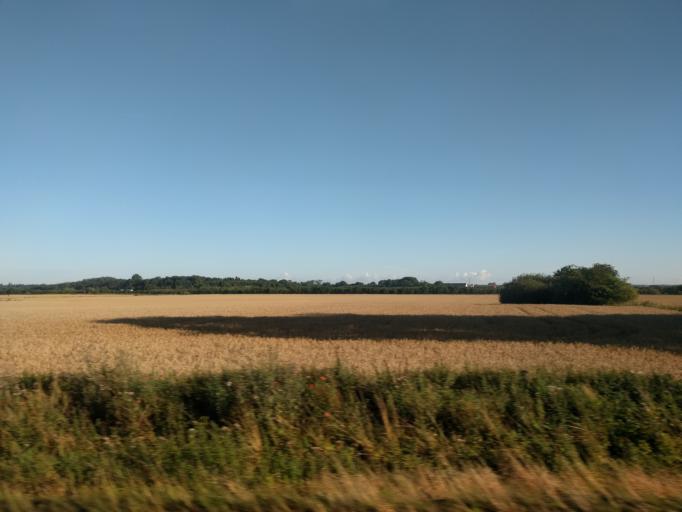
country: DK
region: Zealand
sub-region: Soro Kommune
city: Frederiksberg
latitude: 55.4434
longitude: 11.6746
